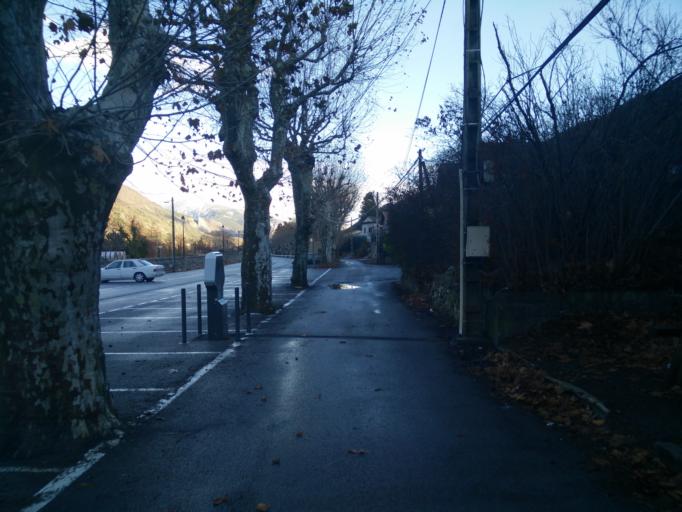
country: FR
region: Provence-Alpes-Cote d'Azur
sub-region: Departement des Alpes-Maritimes
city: Puget-Theniers
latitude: 43.9488
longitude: 6.8124
